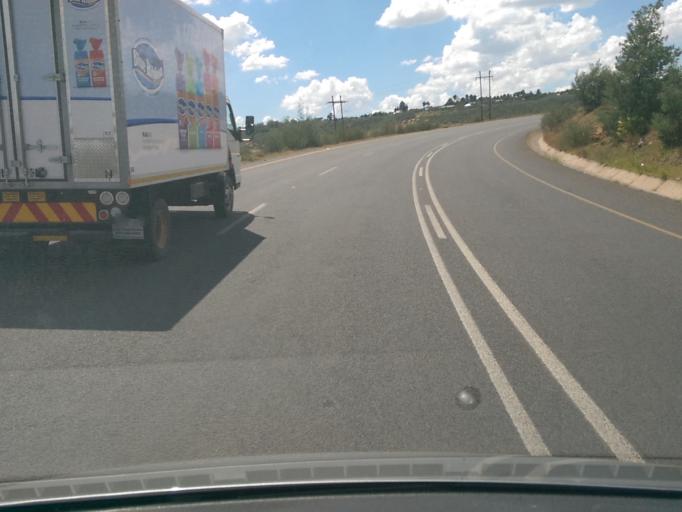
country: LS
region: Maseru
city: Maseru
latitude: -29.3999
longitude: 27.5287
